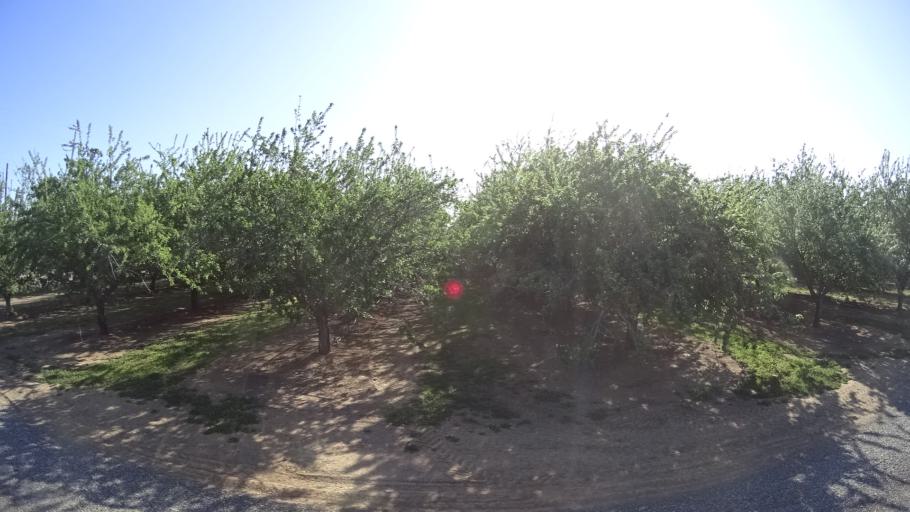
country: US
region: California
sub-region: Glenn County
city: Hamilton City
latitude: 39.7753
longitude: -122.1041
